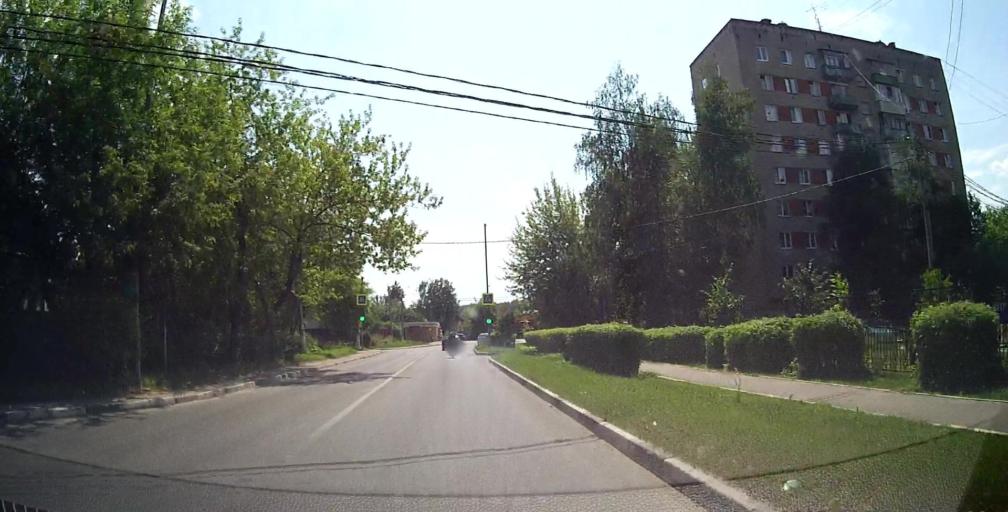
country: RU
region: Moskovskaya
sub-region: Podol'skiy Rayon
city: Podol'sk
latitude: 55.4120
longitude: 37.5252
